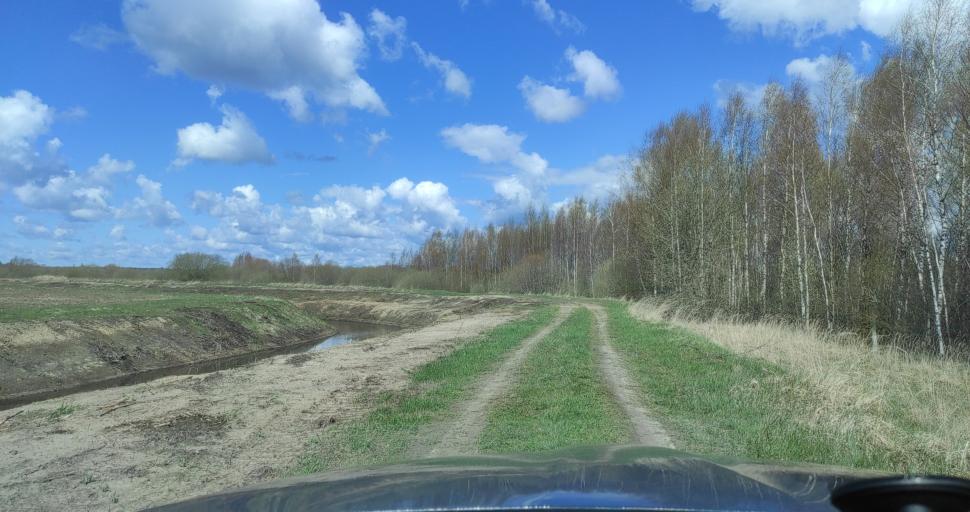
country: LV
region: Kuldigas Rajons
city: Kuldiga
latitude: 56.8729
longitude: 21.7894
